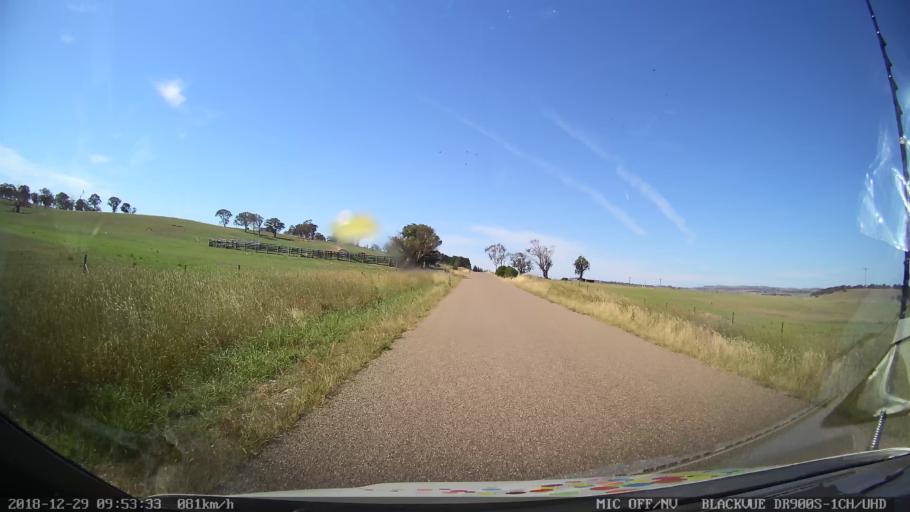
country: AU
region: New South Wales
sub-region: Goulburn Mulwaree
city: Goulburn
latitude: -34.7531
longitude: 149.4692
